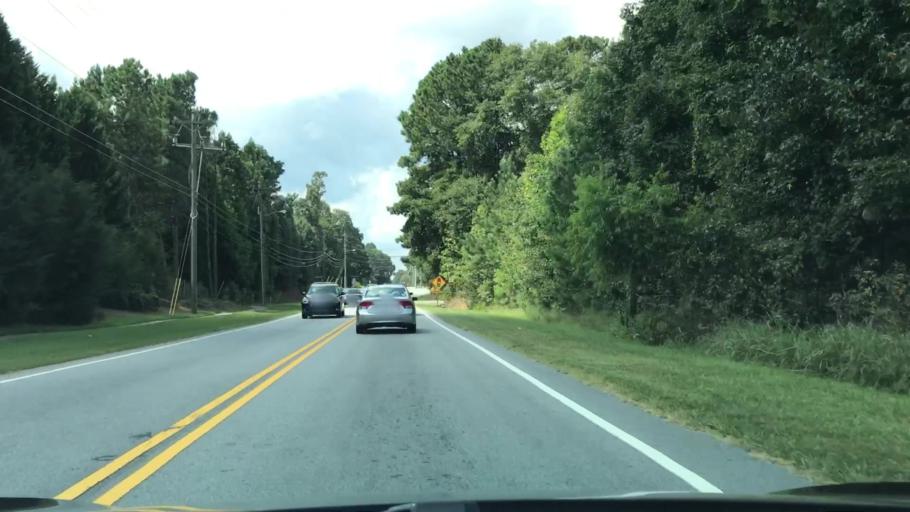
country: US
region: Georgia
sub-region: Gwinnett County
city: Lawrenceville
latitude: 33.9497
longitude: -84.0619
